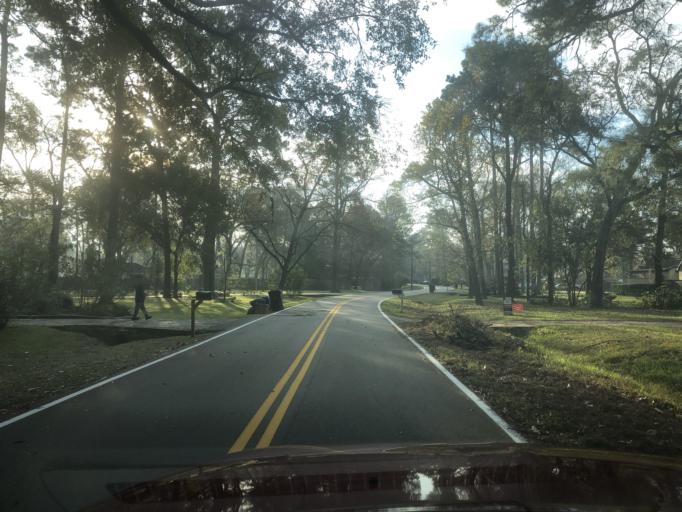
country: US
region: Texas
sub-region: Harris County
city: Spring
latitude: 30.0138
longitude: -95.4768
